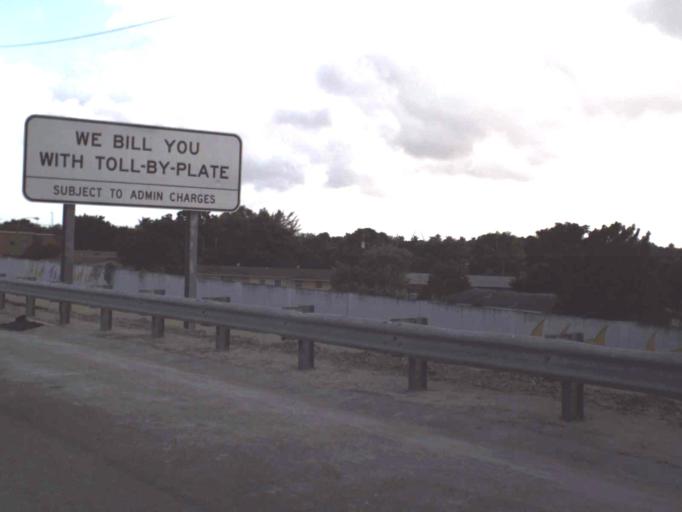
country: US
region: Florida
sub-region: Miami-Dade County
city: Scott Lake
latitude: 25.9412
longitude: -80.2224
